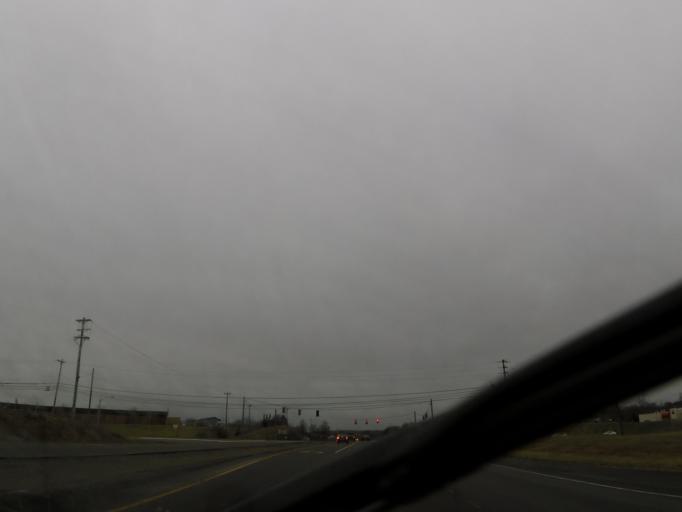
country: US
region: Kentucky
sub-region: Lincoln County
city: Stanford
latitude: 37.5416
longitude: -84.6535
